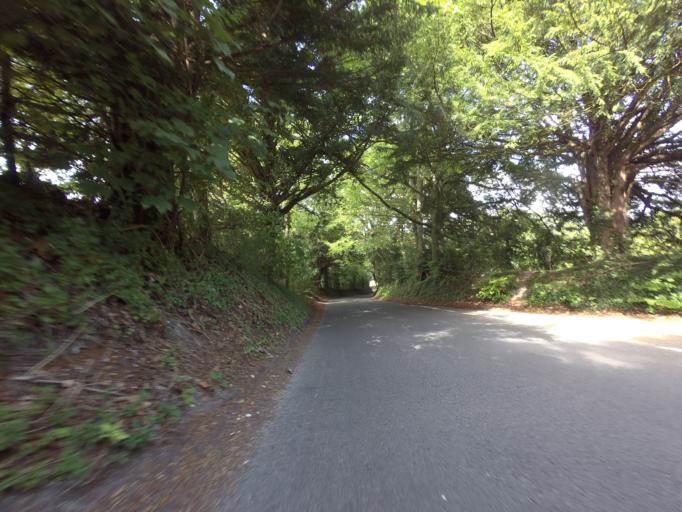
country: GB
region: England
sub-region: Kent
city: Shoreham
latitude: 51.3414
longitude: 0.1765
